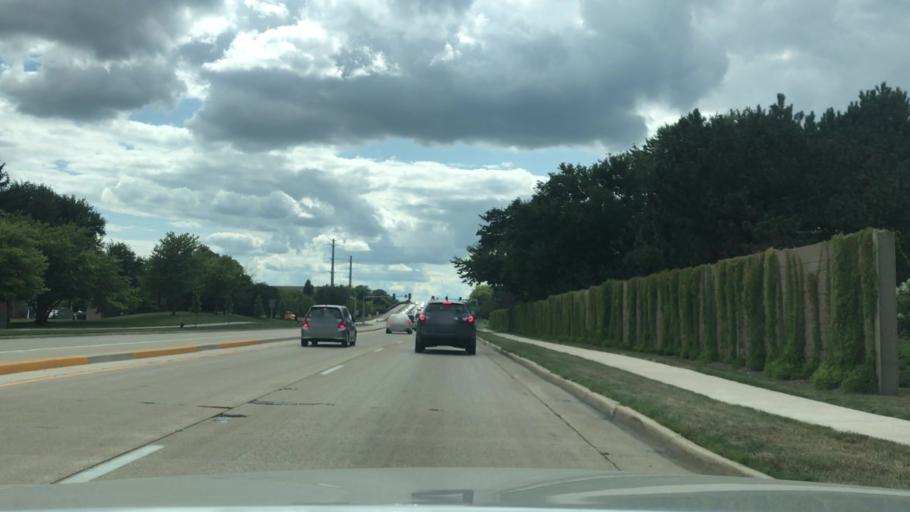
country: US
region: Illinois
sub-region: DuPage County
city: Naperville
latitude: 41.7465
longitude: -88.2279
